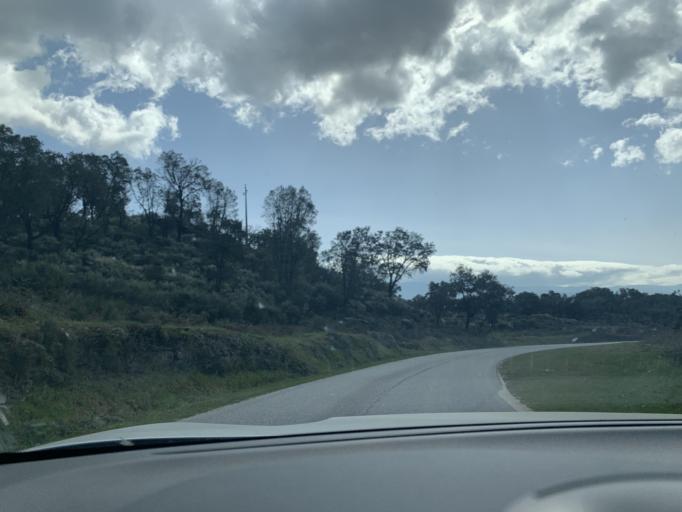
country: PT
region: Guarda
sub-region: Fornos de Algodres
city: Fornos de Algodres
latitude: 40.5753
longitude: -7.5945
